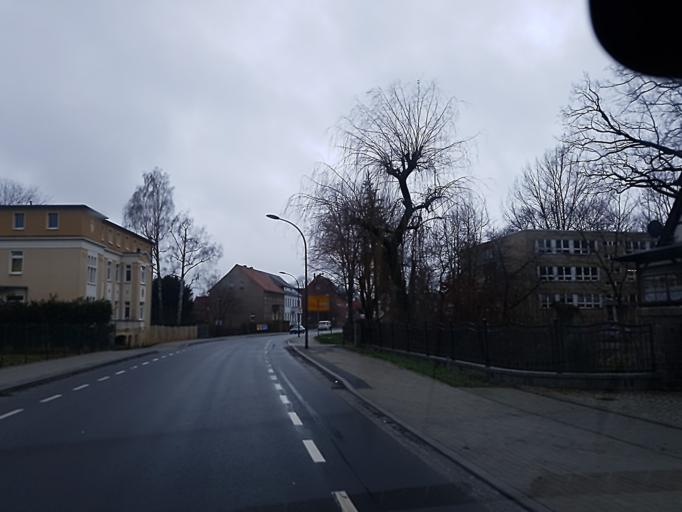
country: DE
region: Brandenburg
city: Finsterwalde
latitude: 51.6266
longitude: 13.7162
